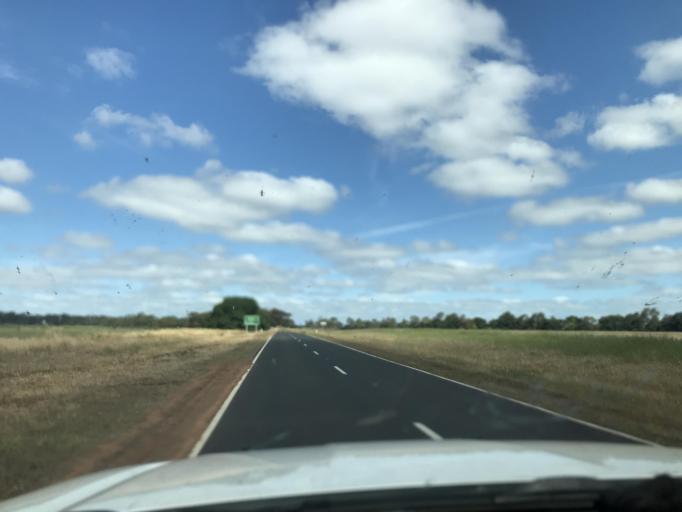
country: AU
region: South Australia
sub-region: Naracoorte and Lucindale
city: Naracoorte
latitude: -37.0175
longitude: 141.3009
